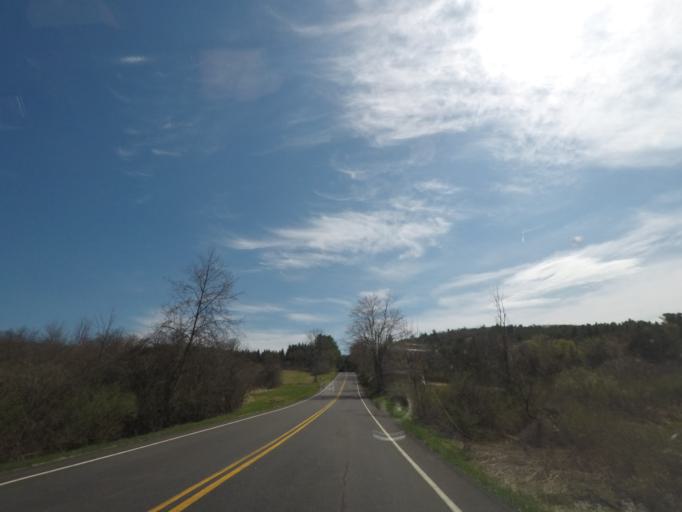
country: US
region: New York
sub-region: Columbia County
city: Chatham
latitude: 42.3818
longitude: -73.5300
